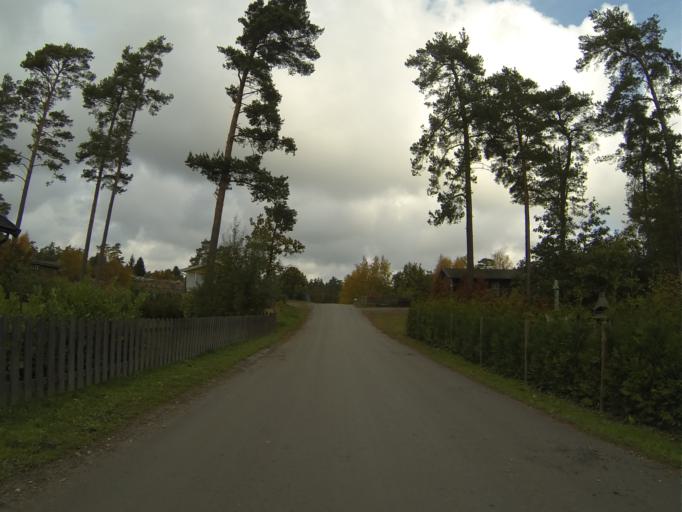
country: SE
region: Skane
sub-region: Sjobo Kommun
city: Sjoebo
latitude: 55.6328
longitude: 13.6455
